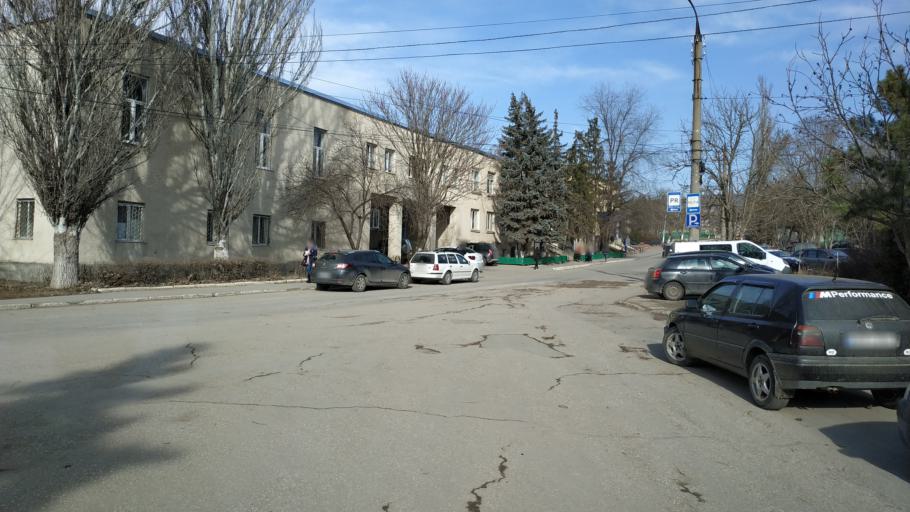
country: MD
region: Nisporeni
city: Nisporeni
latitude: 47.0794
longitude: 28.1885
